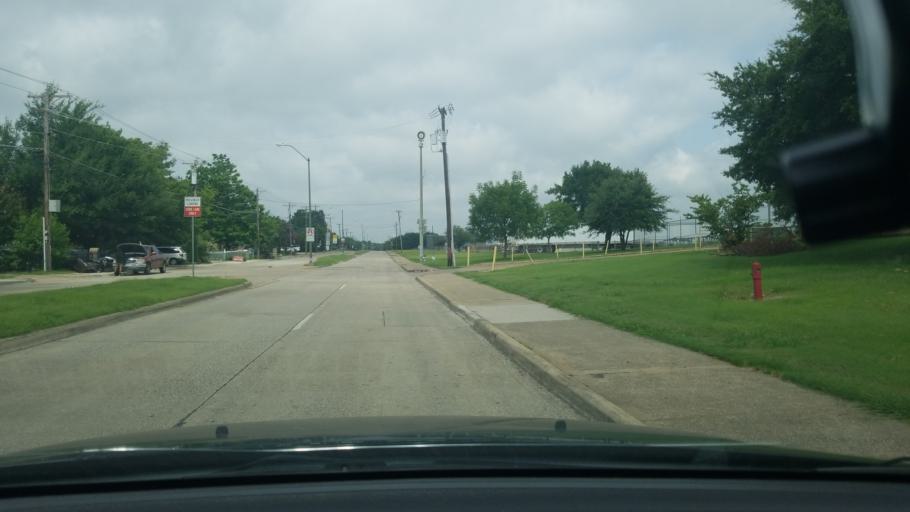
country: US
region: Texas
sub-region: Dallas County
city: Balch Springs
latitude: 32.7782
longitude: -96.6898
